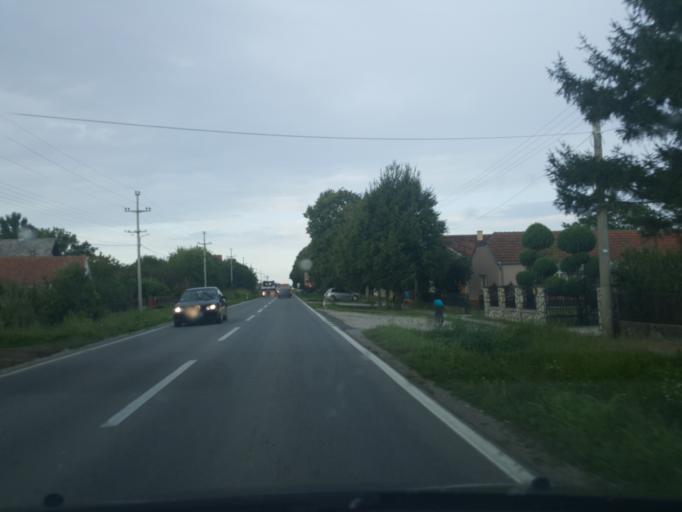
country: RS
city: Ribari
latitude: 44.7238
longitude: 19.4488
